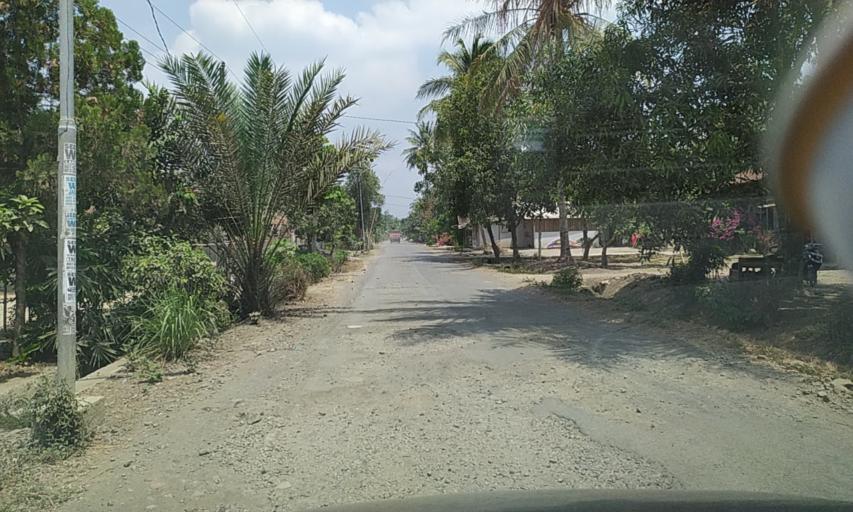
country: ID
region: Central Java
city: Kemantren Satu
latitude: -7.5479
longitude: 108.9184
